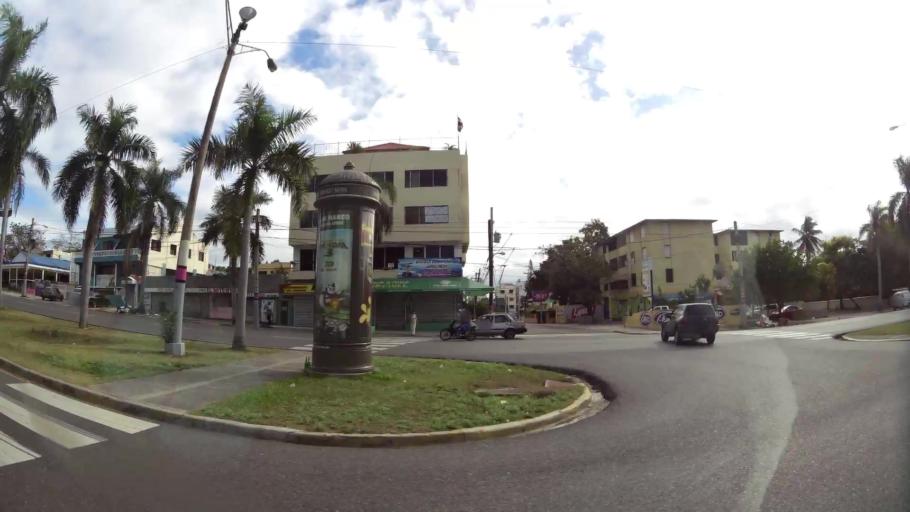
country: DO
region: Nacional
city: La Julia
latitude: 18.4543
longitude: -69.9297
